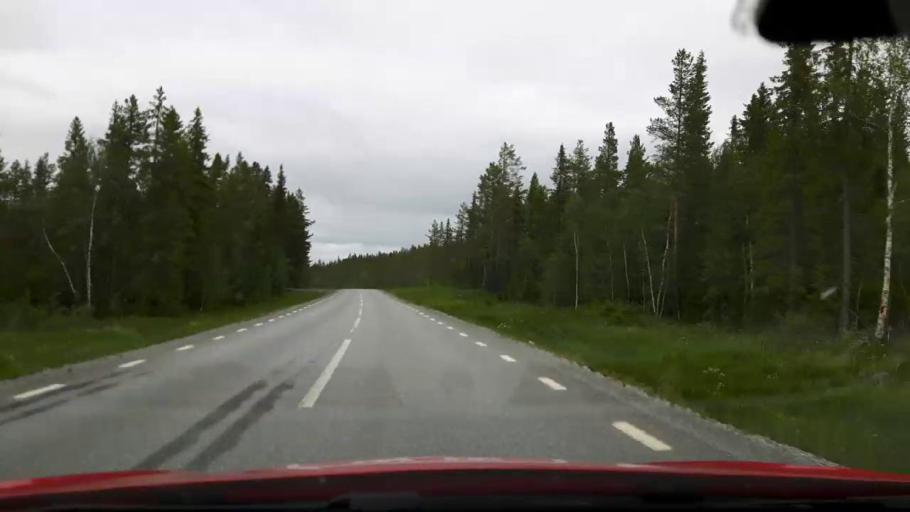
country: SE
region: Jaemtland
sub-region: OEstersunds Kommun
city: Lit
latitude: 63.6930
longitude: 14.6816
